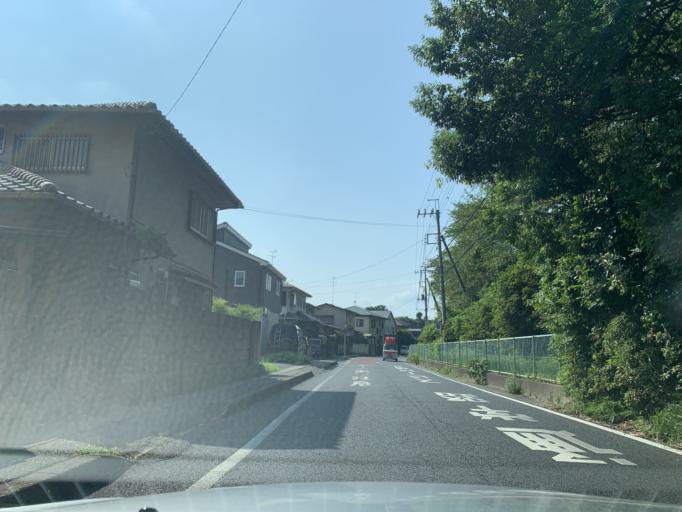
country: JP
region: Chiba
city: Kashiwa
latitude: 35.8423
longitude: 139.9385
